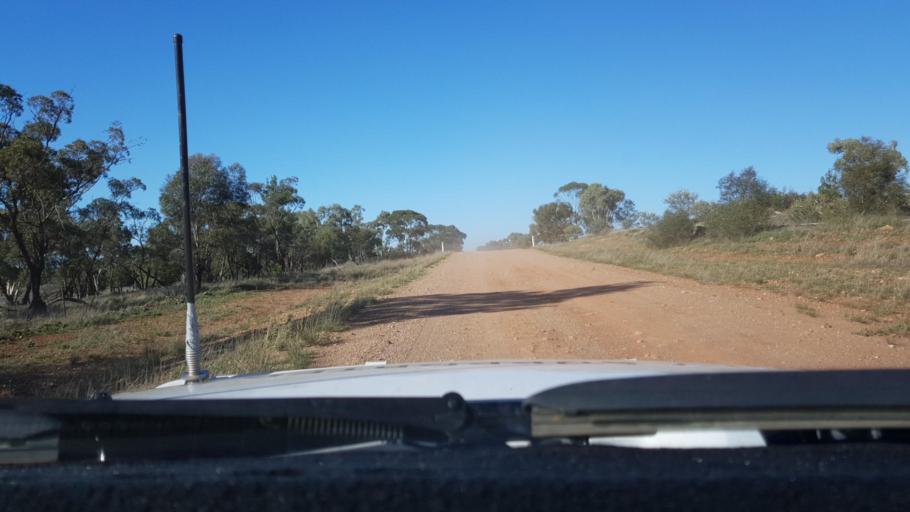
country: AU
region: New South Wales
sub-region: Cobar
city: Cobar
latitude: -31.5919
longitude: 146.3258
